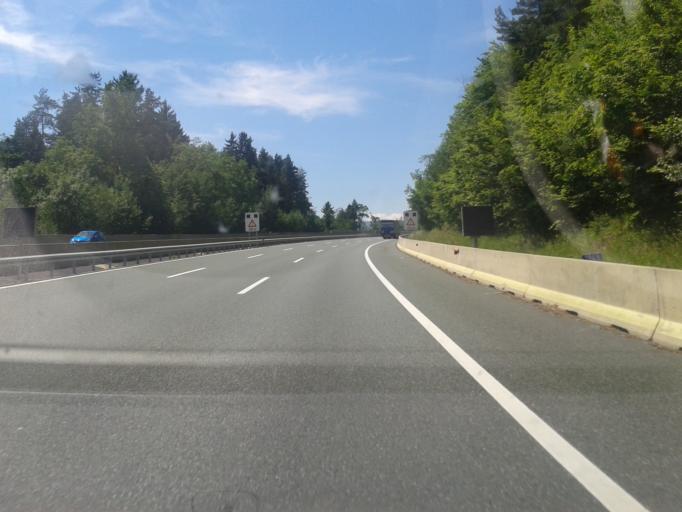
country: AT
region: Styria
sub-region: Politischer Bezirk Deutschlandsberg
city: Gundersdorf
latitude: 46.9547
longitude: 15.2392
